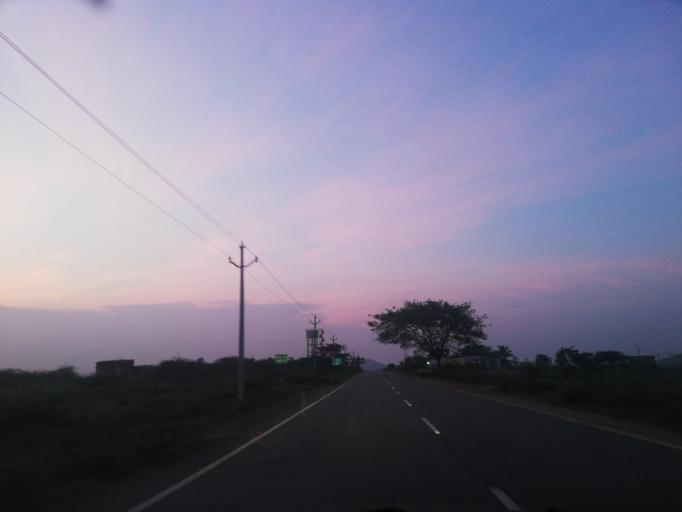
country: IN
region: Andhra Pradesh
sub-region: Guntur
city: Macherla
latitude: 16.6905
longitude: 79.2497
